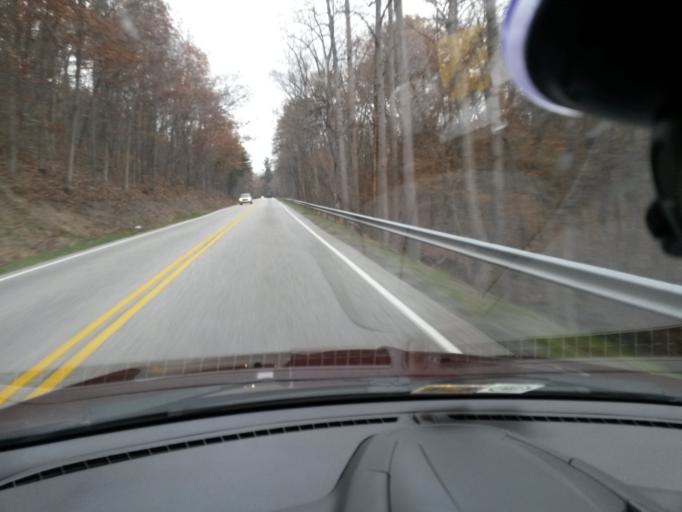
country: US
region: Virginia
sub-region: Rockbridge County
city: Glasgow
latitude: 37.6696
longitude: -79.4150
